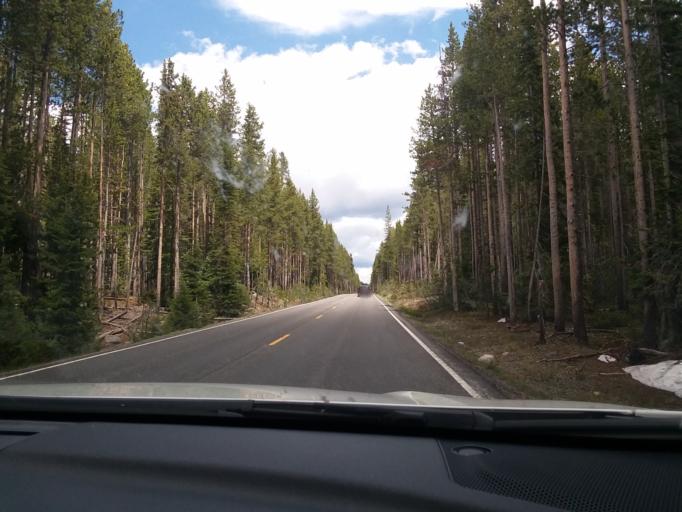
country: US
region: Idaho
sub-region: Teton County
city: Driggs
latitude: 44.1782
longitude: -110.6605
